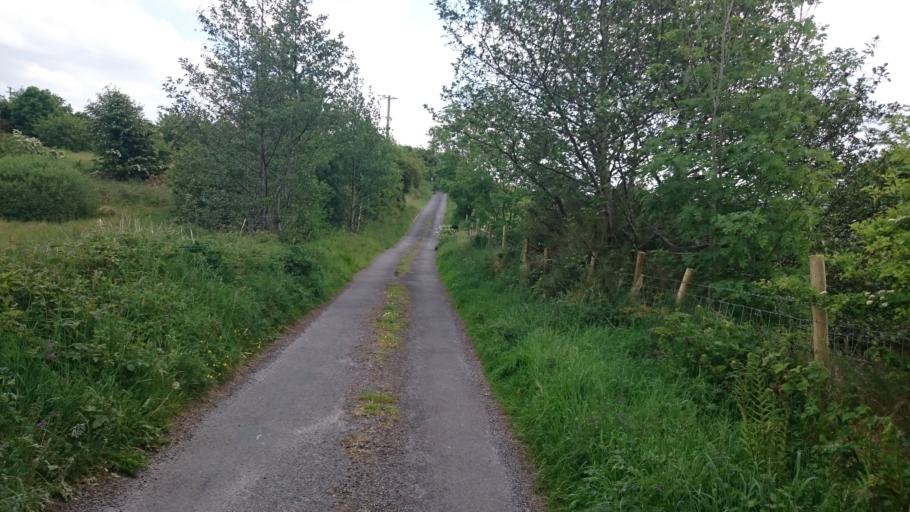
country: IE
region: Connaught
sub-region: Sligo
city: Inishcrone
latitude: 54.1112
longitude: -9.0184
